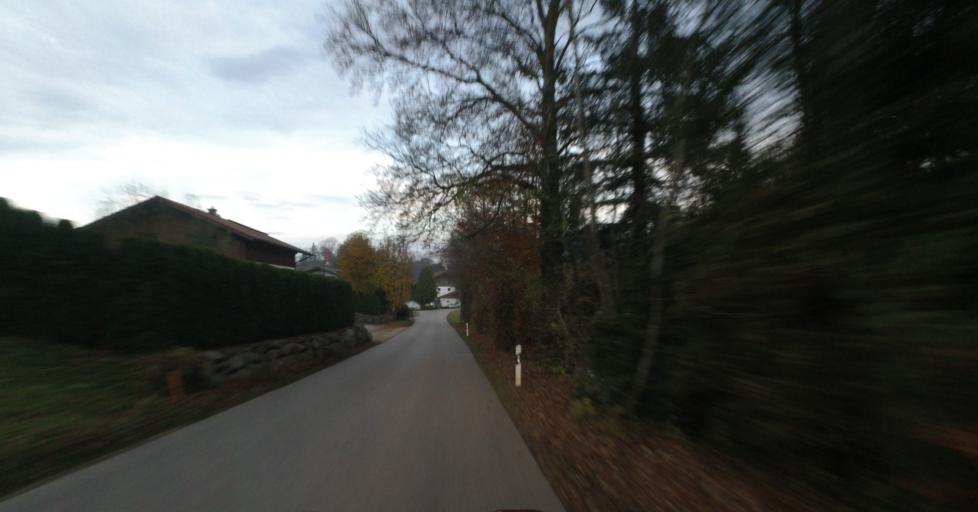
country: DE
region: Bavaria
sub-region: Upper Bavaria
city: Prien am Chiemsee
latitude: 47.8406
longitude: 12.3212
